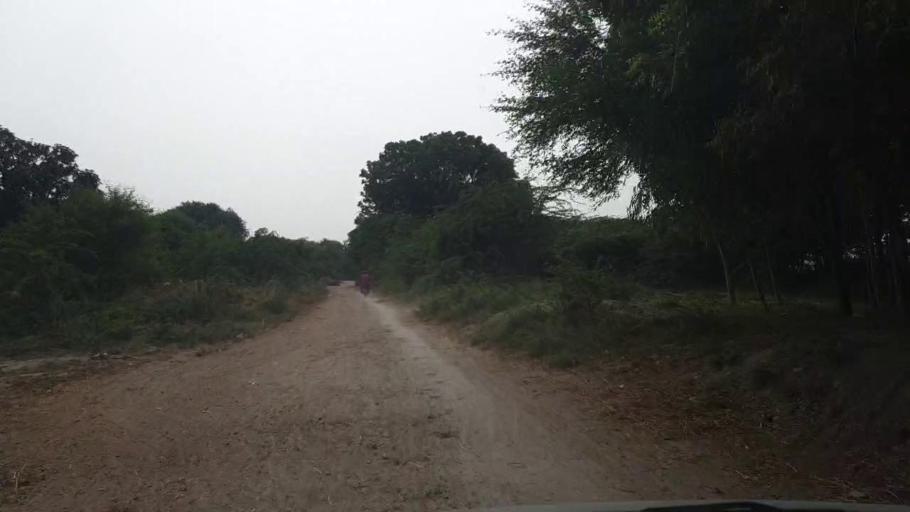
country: PK
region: Sindh
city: Matli
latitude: 24.9905
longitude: 68.7028
